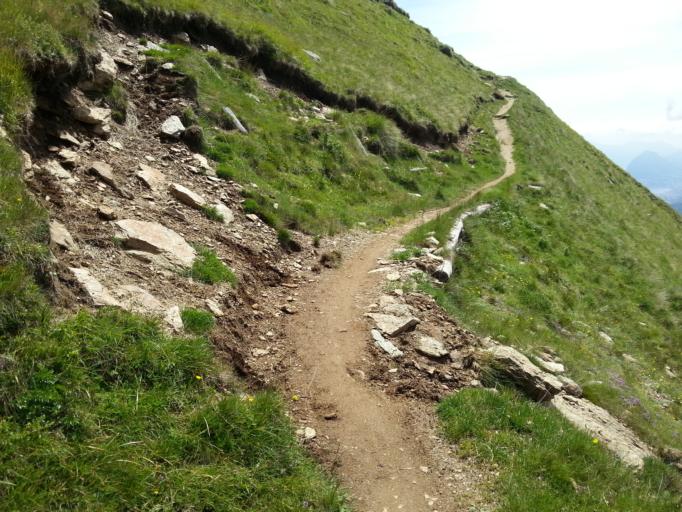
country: CH
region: Ticino
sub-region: Lugano District
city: Tesserete
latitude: 46.0981
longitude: 8.9850
